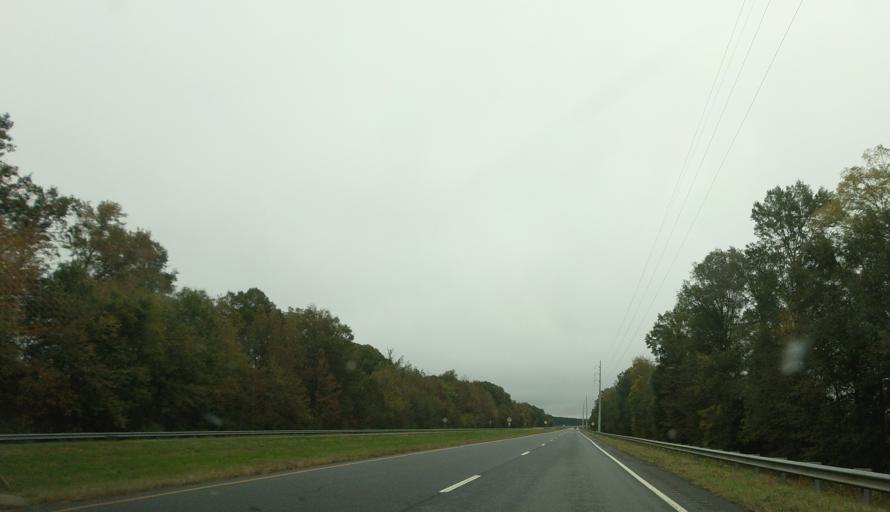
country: US
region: Georgia
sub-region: Taylor County
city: Reynolds
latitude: 32.5410
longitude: -84.0211
